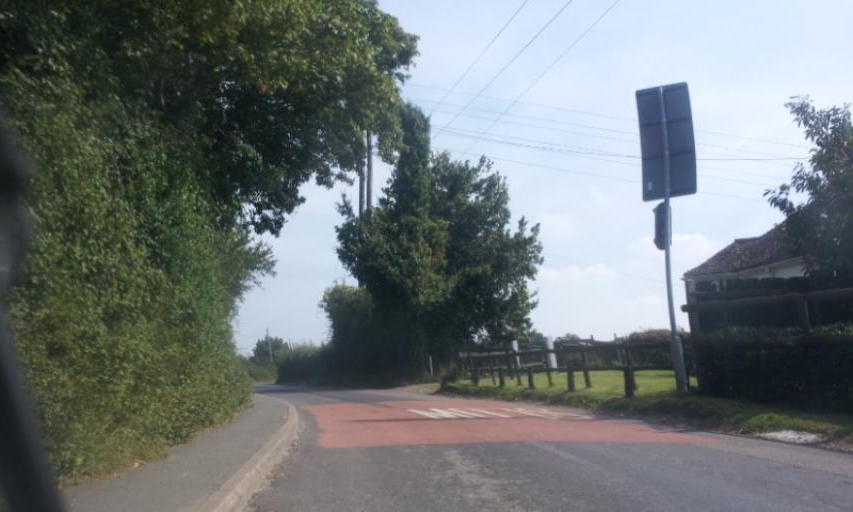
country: GB
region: England
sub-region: Kent
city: Newington
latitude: 51.3378
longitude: 0.6956
